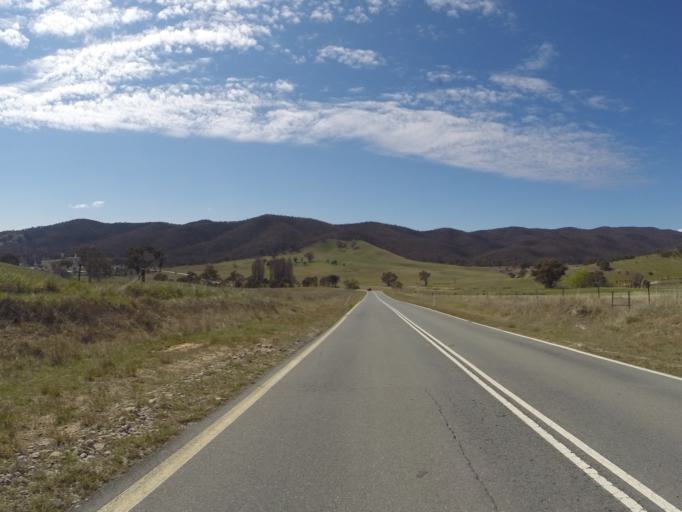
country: AU
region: Australian Capital Territory
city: Macarthur
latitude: -35.4116
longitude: 148.9771
